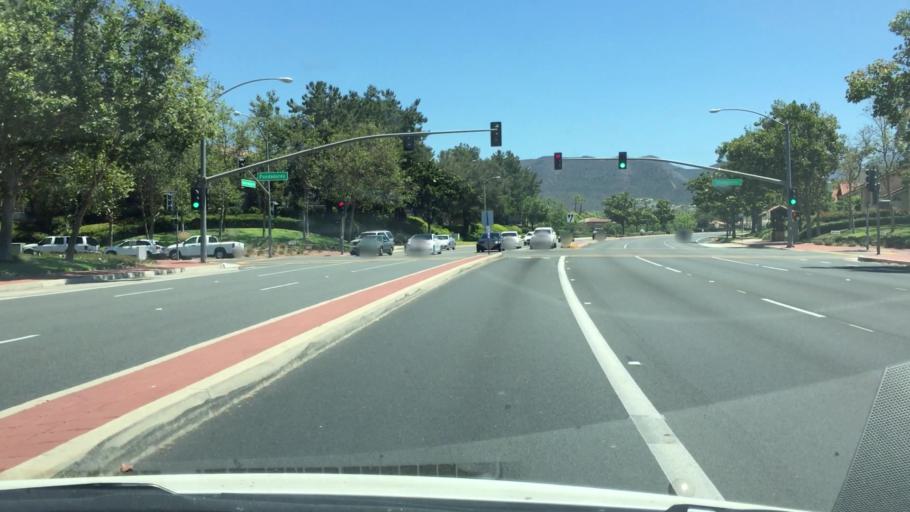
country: US
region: California
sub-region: Orange County
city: Trabuco Canyon
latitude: 33.6483
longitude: -117.5867
